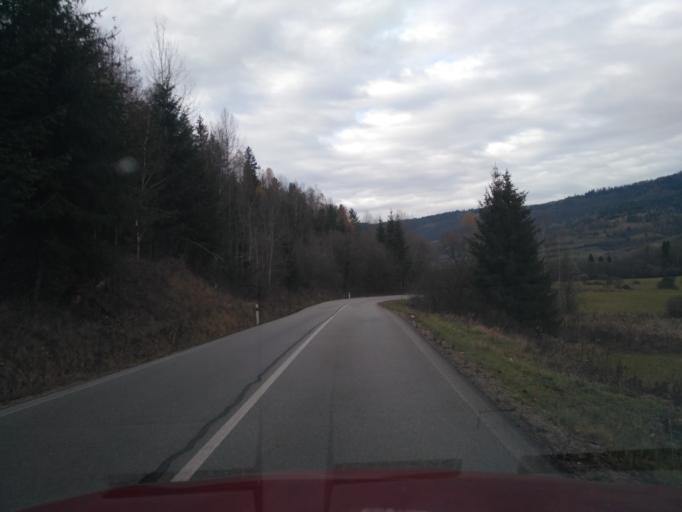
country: SK
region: Kosicky
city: Spisska Nova Ves
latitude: 48.8216
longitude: 20.6576
